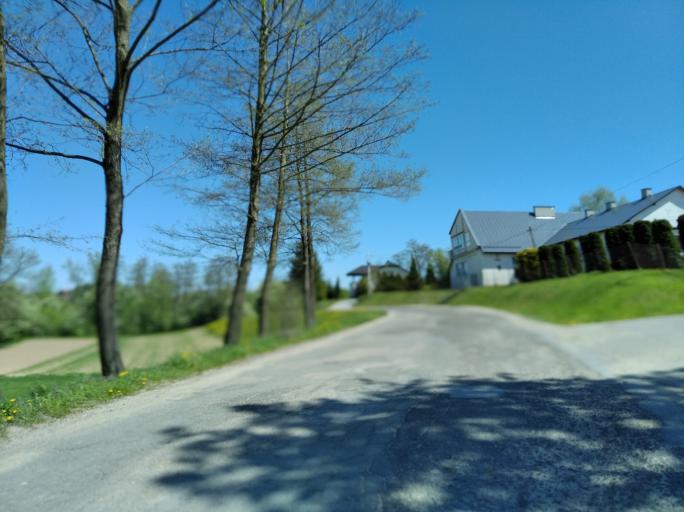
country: PL
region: Subcarpathian Voivodeship
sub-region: Powiat debicki
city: Brzostek
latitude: 49.9180
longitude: 21.4441
